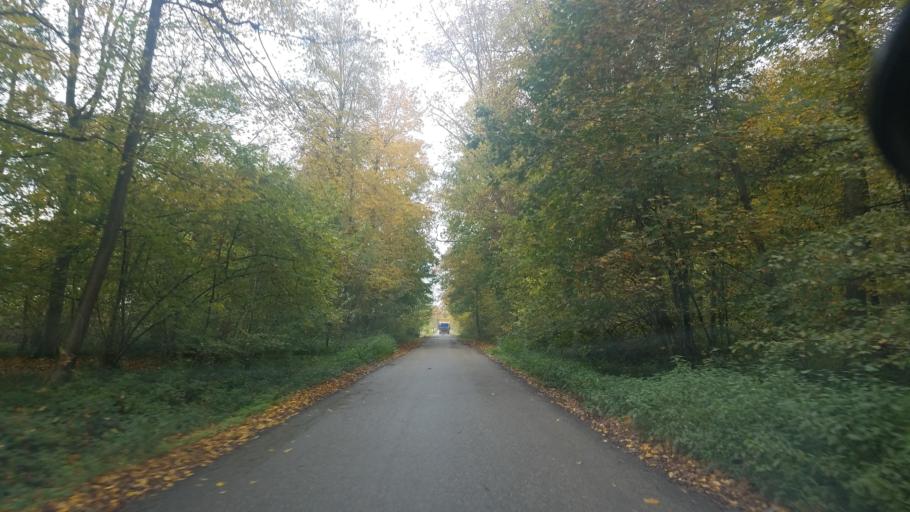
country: DE
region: Baden-Wuerttemberg
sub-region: Freiburg Region
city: Rheinau
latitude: 48.6601
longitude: 8.0010
